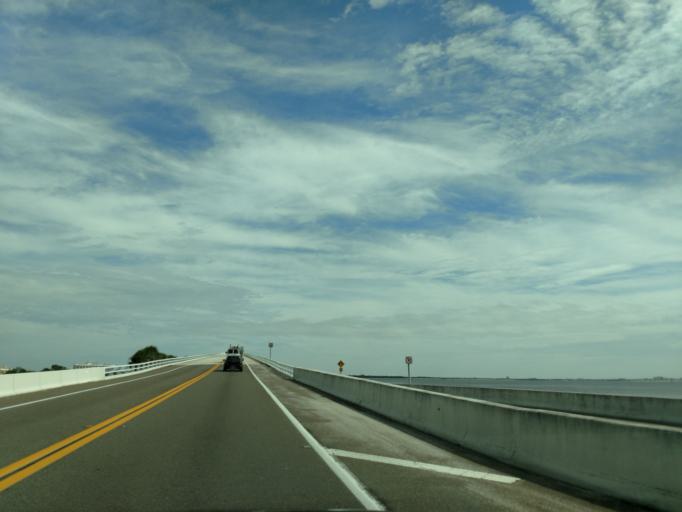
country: US
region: Florida
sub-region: Lee County
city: Punta Rassa
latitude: 26.4814
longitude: -82.0198
